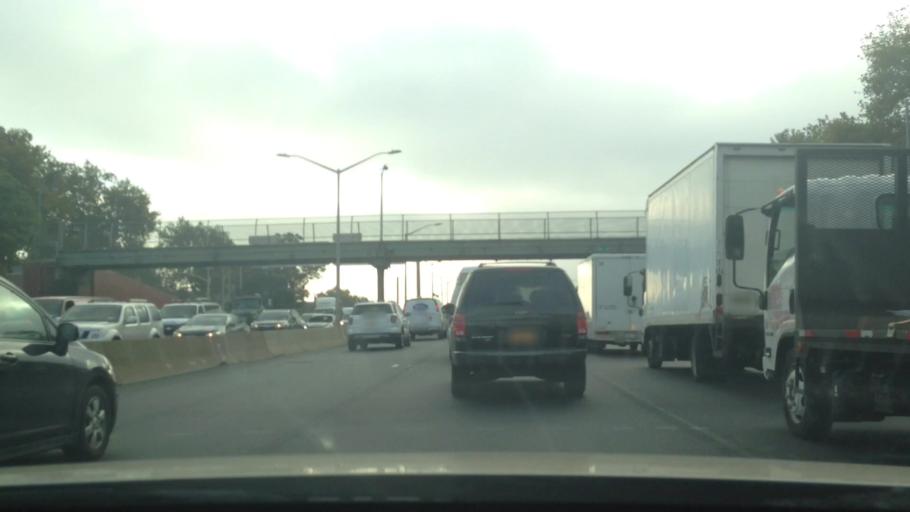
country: US
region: New York
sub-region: Queens County
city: Jamaica
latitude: 40.7430
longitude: -73.8311
